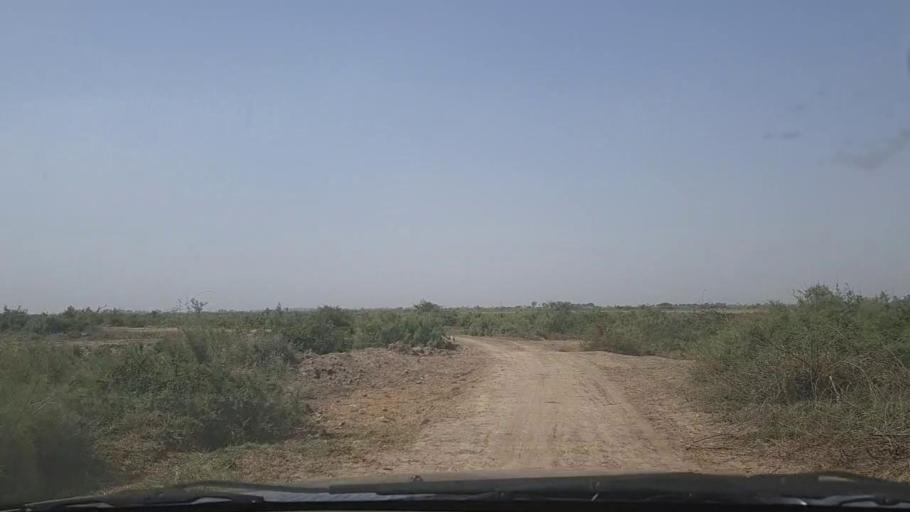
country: PK
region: Sindh
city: Keti Bandar
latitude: 24.2642
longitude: 67.6575
